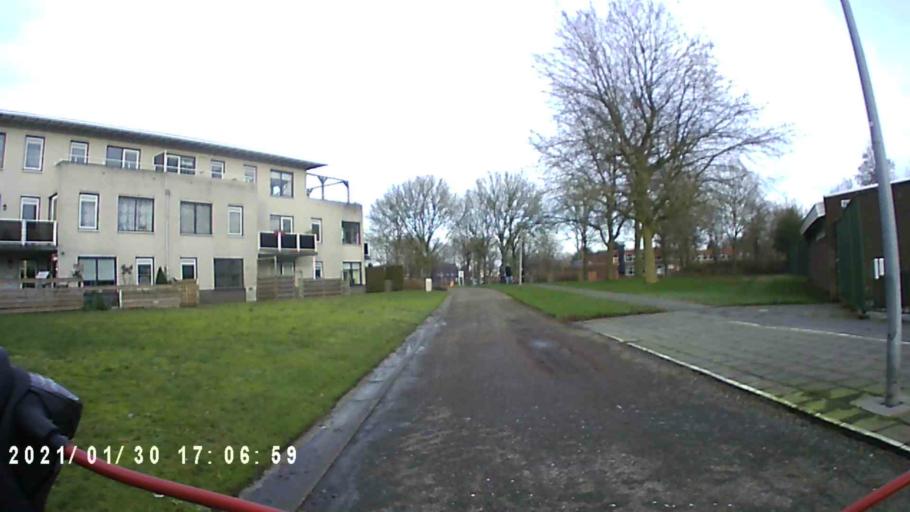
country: NL
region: Groningen
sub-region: Gemeente Leek
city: Leek
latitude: 53.1612
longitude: 6.3663
